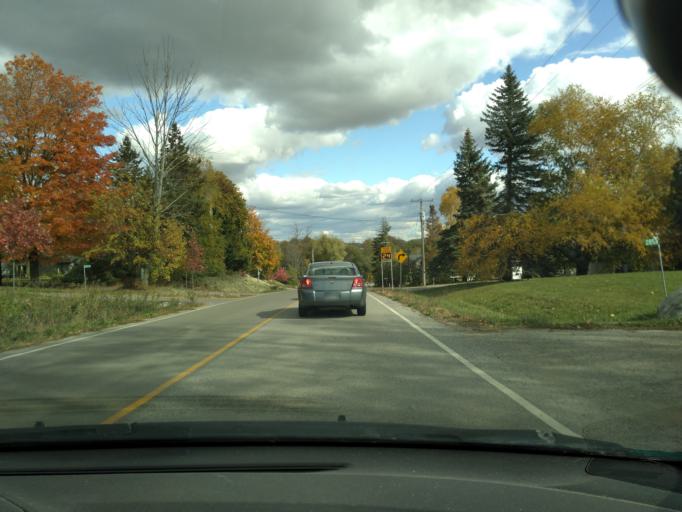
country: CA
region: Ontario
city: Bradford West Gwillimbury
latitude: 44.0849
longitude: -79.5809
